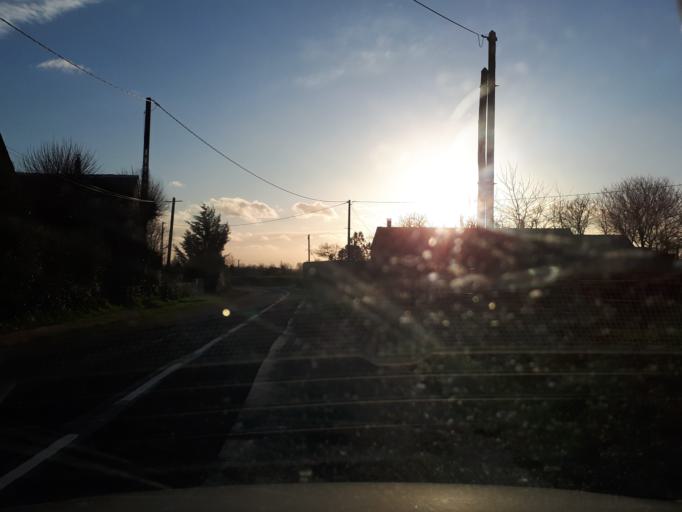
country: FR
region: Pays de la Loire
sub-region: Departement de la Sarthe
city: Ballon
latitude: 48.1659
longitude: 0.2324
